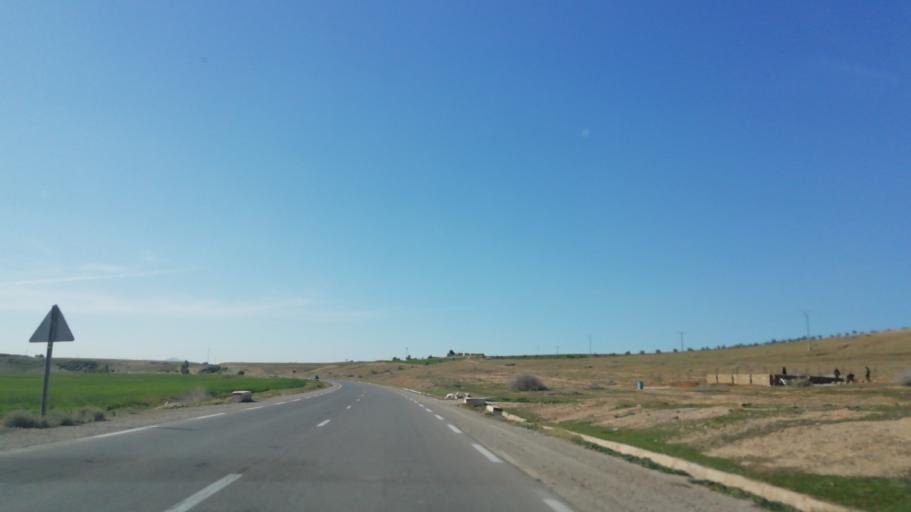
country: DZ
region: Mascara
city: Oued el Abtal
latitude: 35.4523
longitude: 0.7775
